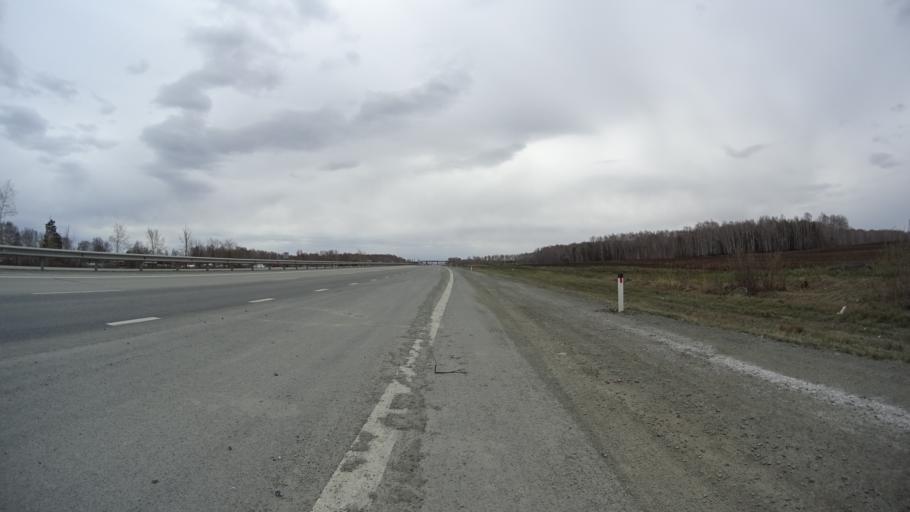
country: RU
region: Chelyabinsk
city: Yemanzhelinka
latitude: 54.8231
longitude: 61.3092
